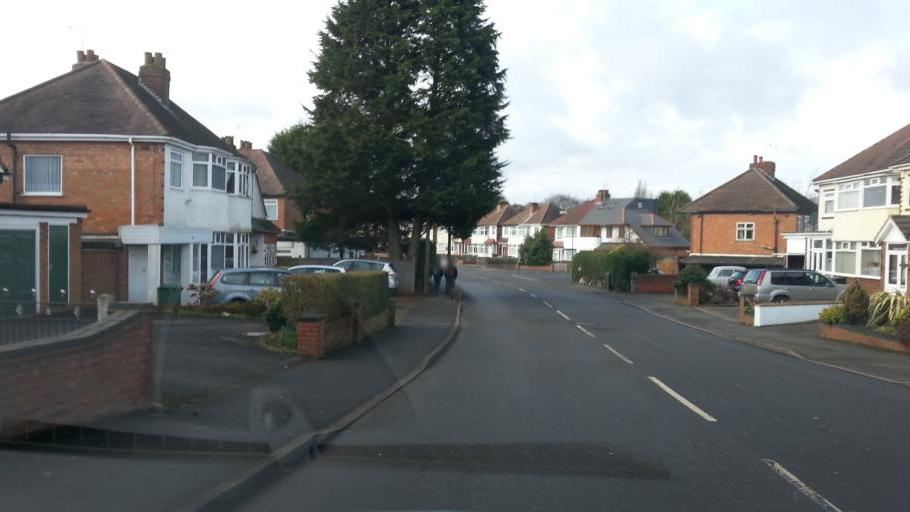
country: GB
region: England
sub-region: City and Borough of Birmingham
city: Acocks Green
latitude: 52.4408
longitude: -1.7928
